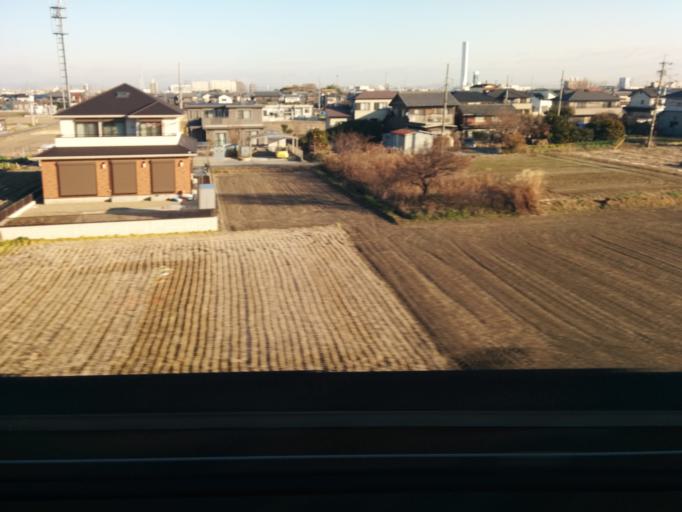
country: JP
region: Aichi
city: Inazawa
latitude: 35.2278
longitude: 136.8059
